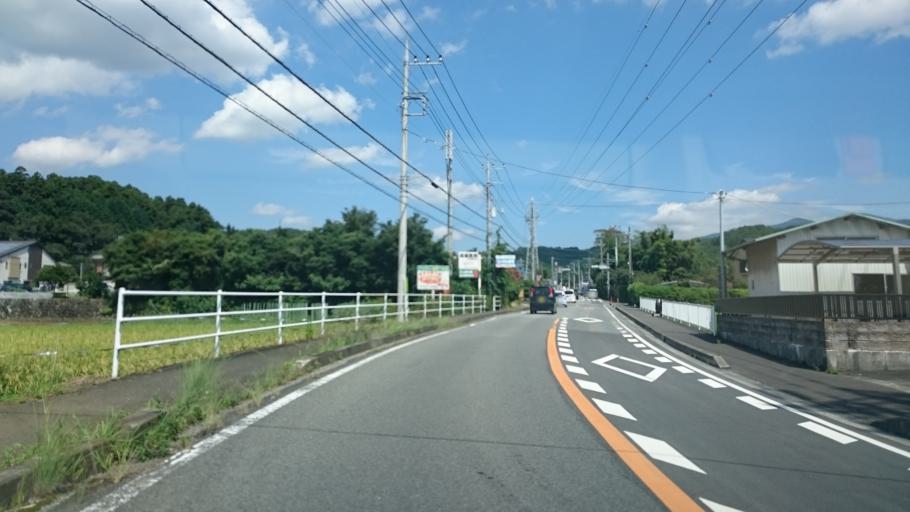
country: JP
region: Shizuoka
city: Mishima
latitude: 35.1931
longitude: 138.9221
